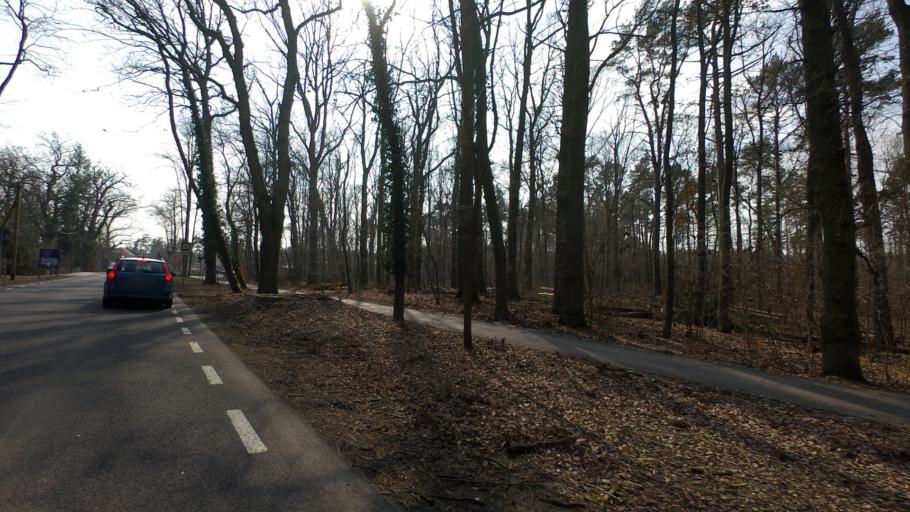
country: DE
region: Brandenburg
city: Werder
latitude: 52.3277
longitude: 12.9275
